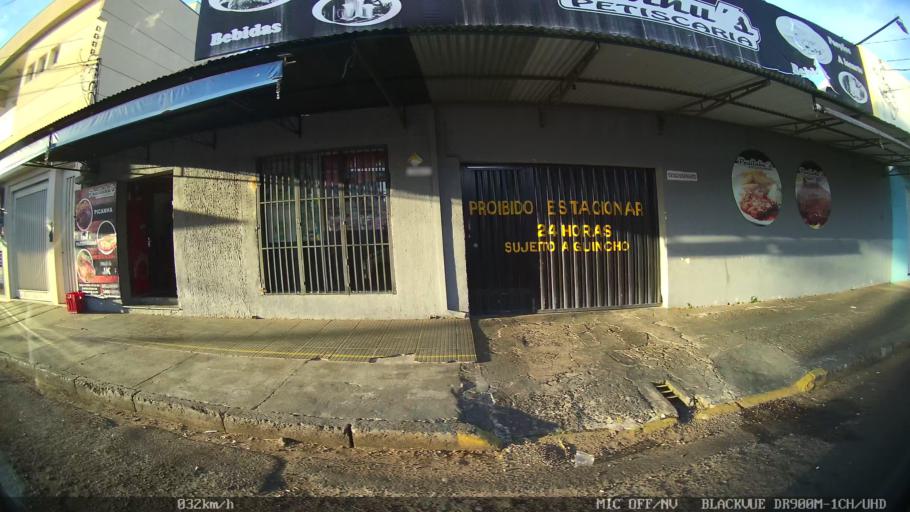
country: BR
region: Sao Paulo
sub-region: Franca
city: Franca
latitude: -20.5278
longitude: -47.3911
